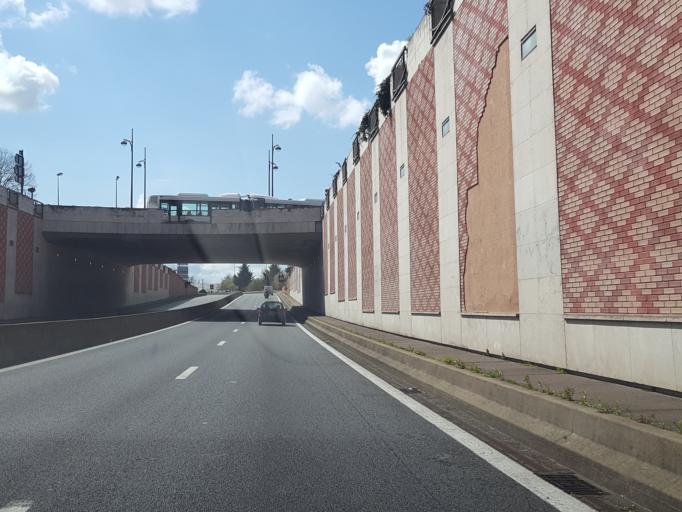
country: FR
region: Centre
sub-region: Departement du Loiret
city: Saint-Jean-de-la-Ruelle
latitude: 47.9156
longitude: 1.8696
